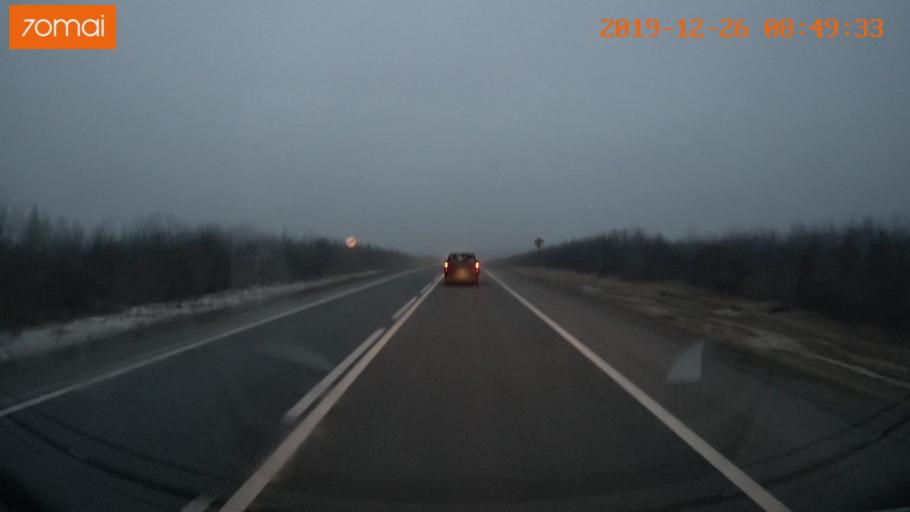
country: RU
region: Jaroslavl
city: Prechistoye
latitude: 58.6502
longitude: 40.3194
